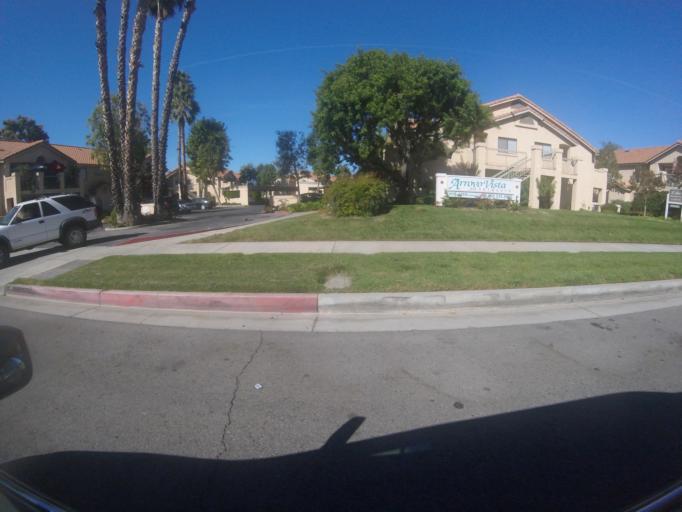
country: US
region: California
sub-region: San Bernardino County
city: Redlands
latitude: 34.0520
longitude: -117.2061
